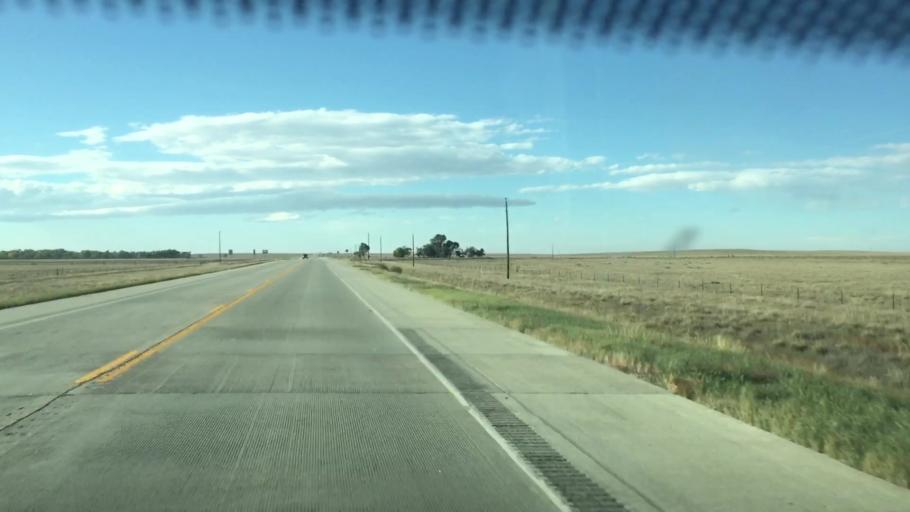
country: US
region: Colorado
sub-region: Lincoln County
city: Hugo
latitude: 39.0483
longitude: -103.3464
